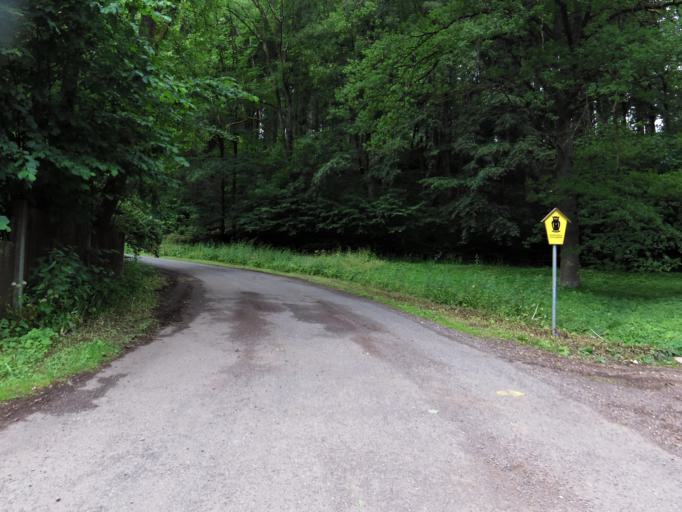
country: DE
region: Thuringia
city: Tabarz
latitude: 50.8663
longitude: 10.5094
